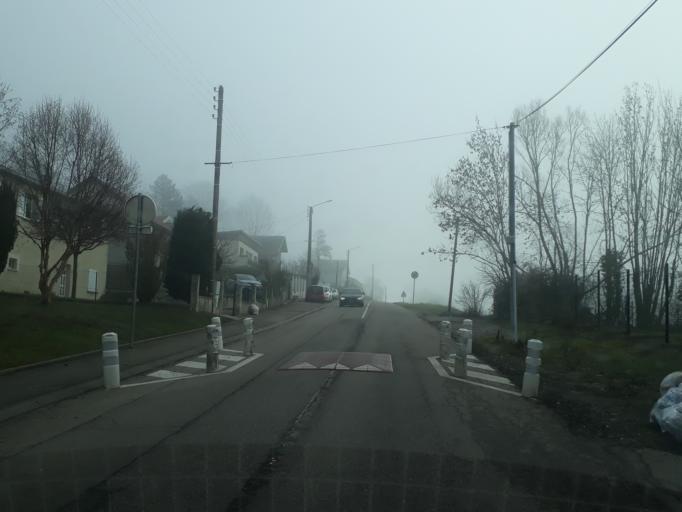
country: FR
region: Lorraine
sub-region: Departement de Meurthe-et-Moselle
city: Bouxieres-aux-Dames
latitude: 48.7482
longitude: 6.1748
